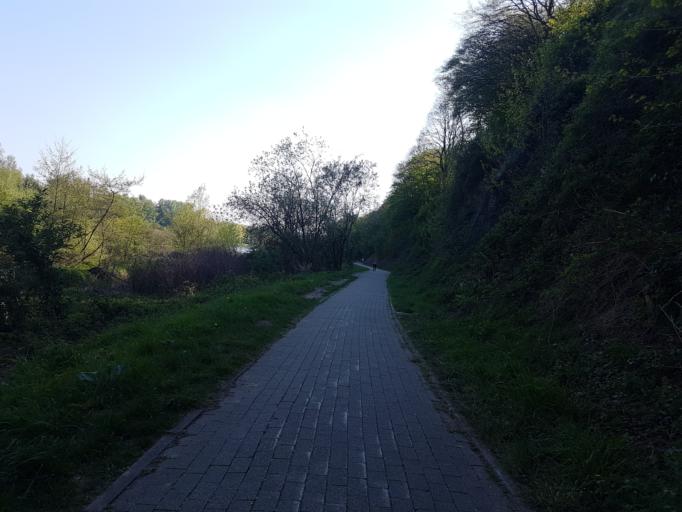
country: DE
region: North Rhine-Westphalia
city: Hattingen
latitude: 51.4179
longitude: 7.1841
